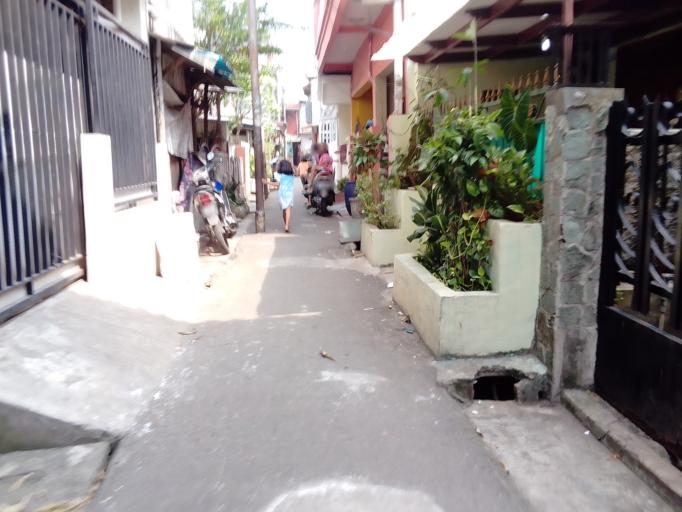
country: ID
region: Jakarta Raya
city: Jakarta
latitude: -6.1931
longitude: 106.8069
